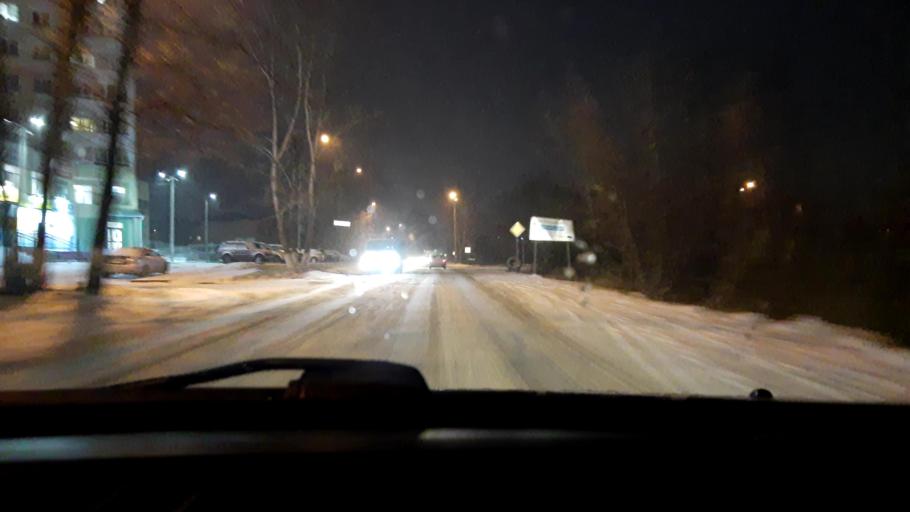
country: RU
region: Nizjnij Novgorod
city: Bor
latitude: 56.3335
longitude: 44.1072
